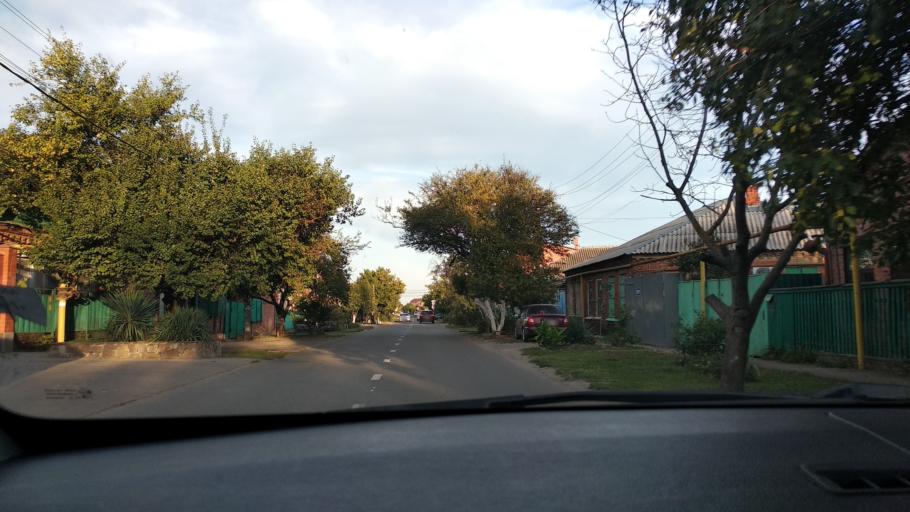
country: RU
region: Krasnodarskiy
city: Krasnodar
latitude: 45.0172
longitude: 39.0020
